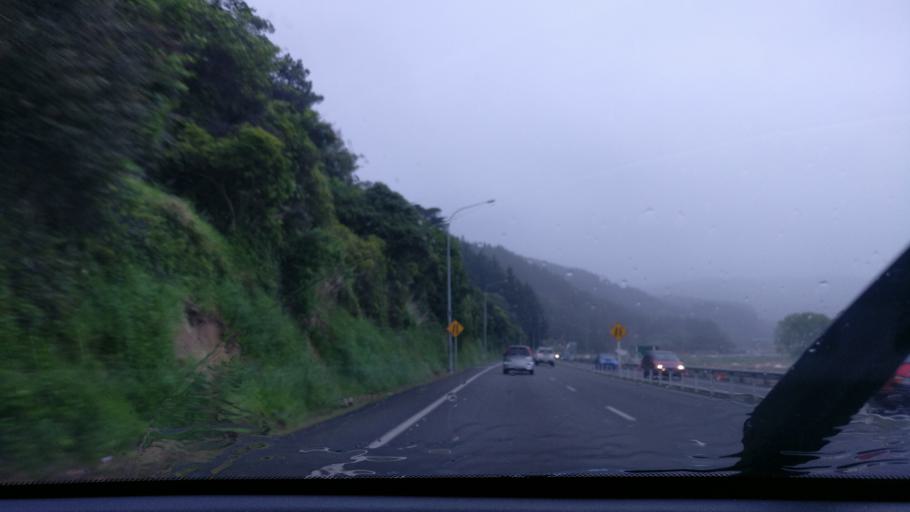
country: NZ
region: Wellington
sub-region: Kapiti Coast District
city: Paraparaumu
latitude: -40.9771
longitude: 174.9781
